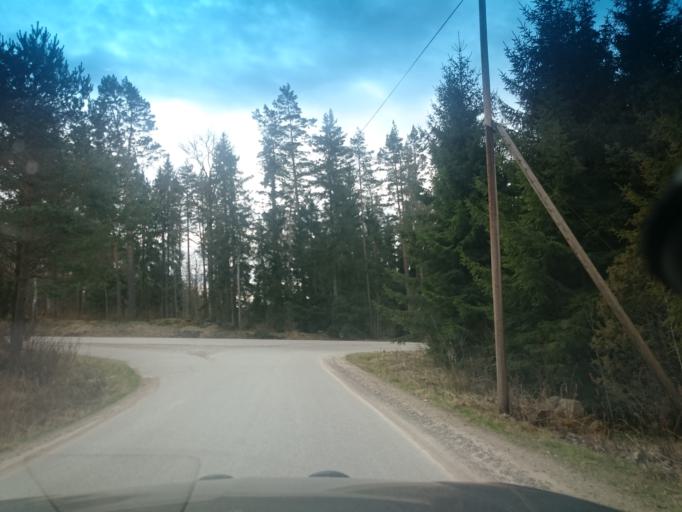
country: SE
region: Joenkoeping
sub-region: Vetlanda Kommun
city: Vetlanda
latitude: 57.3219
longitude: 15.1550
